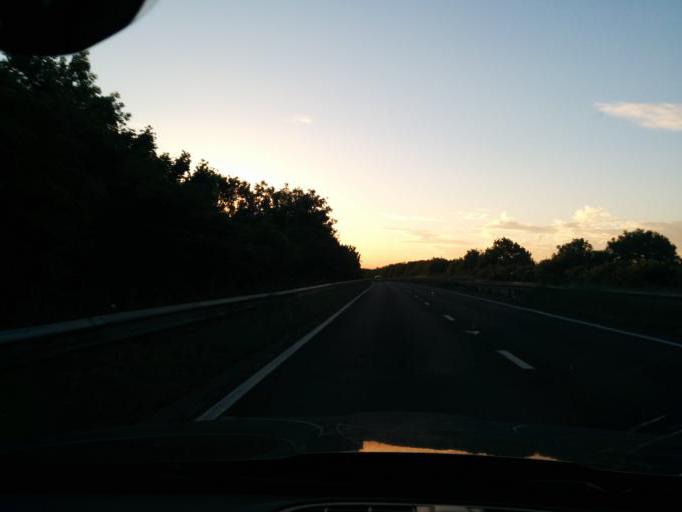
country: GB
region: England
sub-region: Northumberland
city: Seghill
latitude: 55.0598
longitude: -1.5666
